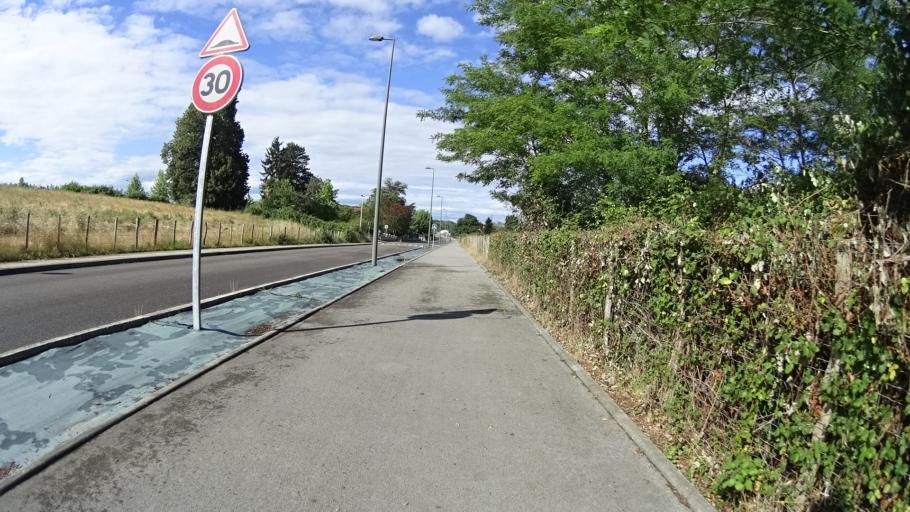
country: FR
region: Aquitaine
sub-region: Departement des Landes
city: Dax
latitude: 43.6973
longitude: -1.0764
